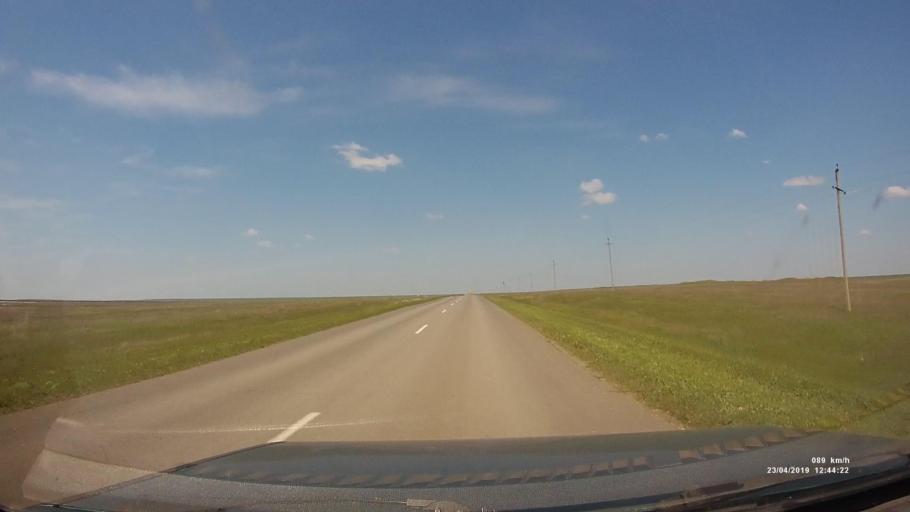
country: RU
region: Kalmykiya
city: Yashalta
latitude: 46.4759
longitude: 42.6478
